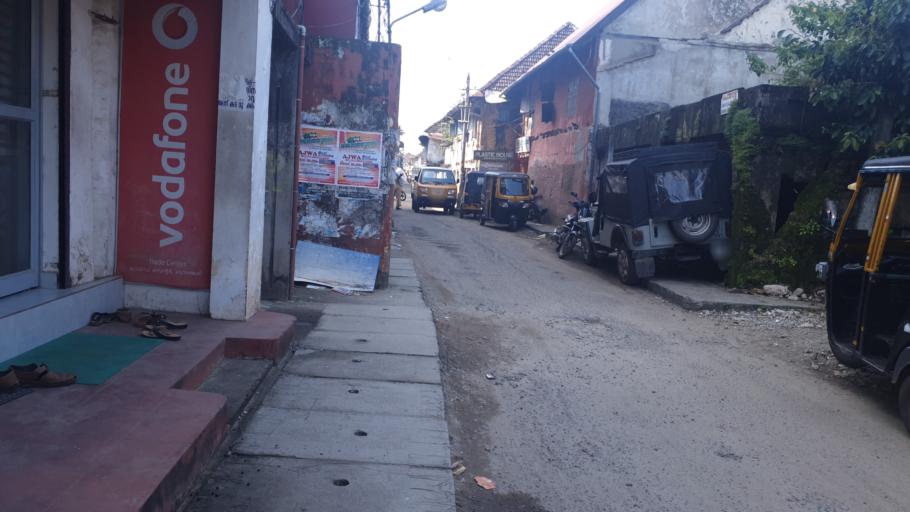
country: IN
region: Kerala
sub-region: Ernakulam
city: Cochin
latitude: 9.9637
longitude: 76.2565
